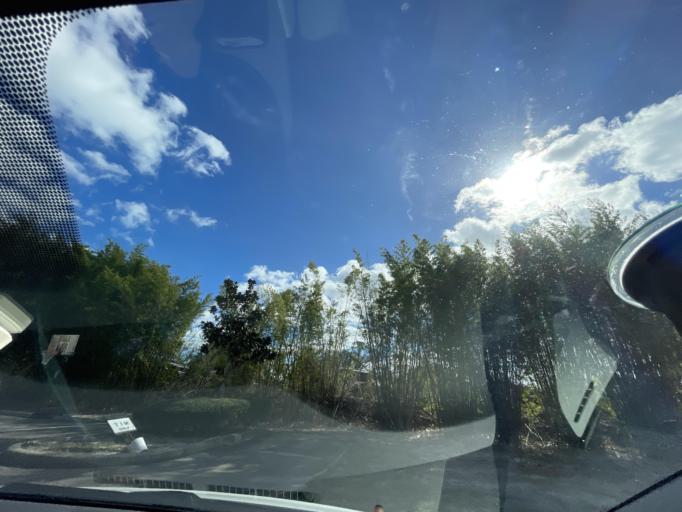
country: US
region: Florida
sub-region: Volusia County
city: South Daytona
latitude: 29.1572
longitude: -81.0249
